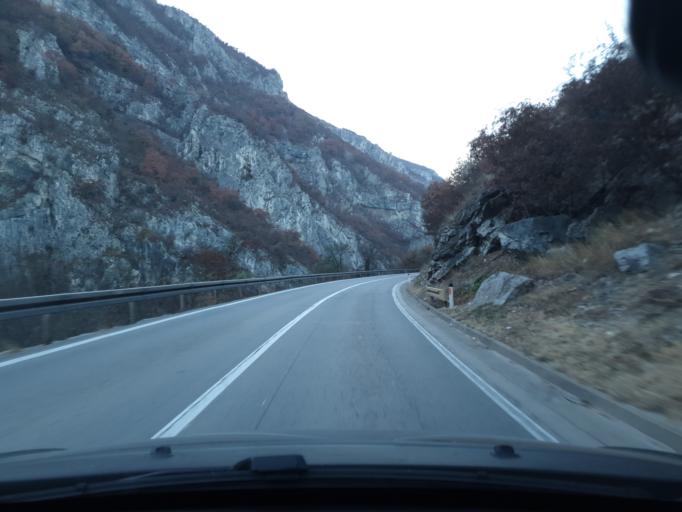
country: RS
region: Central Serbia
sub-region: Nisavski Okrug
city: Svrljig
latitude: 43.3278
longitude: 22.1018
